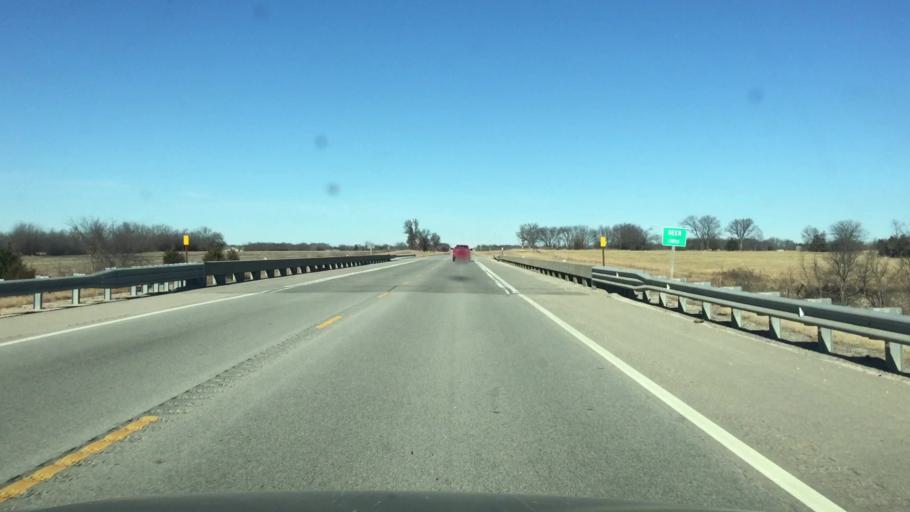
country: US
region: Kansas
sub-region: Allen County
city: Iola
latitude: 37.9858
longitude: -95.3810
